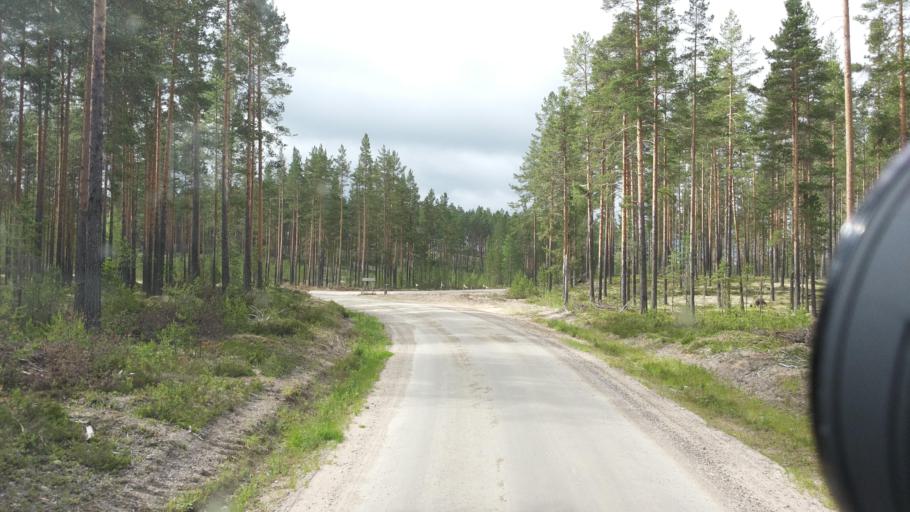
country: SE
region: Gaevleborg
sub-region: Ovanakers Kommun
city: Edsbyn
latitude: 61.5105
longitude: 15.3380
